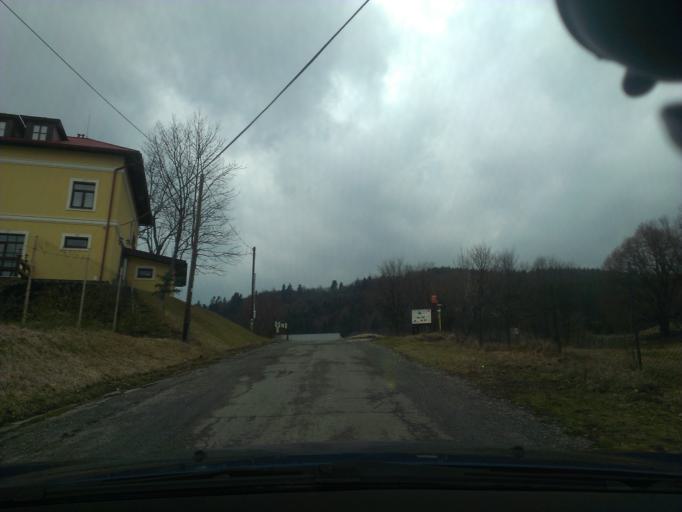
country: SK
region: Banskobystricky
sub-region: Okres Banska Bystrica
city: Banska Stiavnica
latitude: 48.4478
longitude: 18.8754
